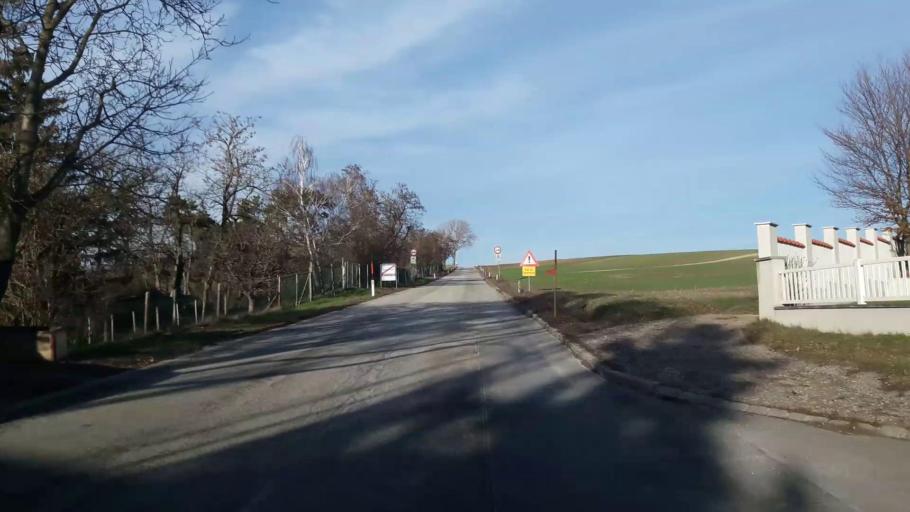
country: AT
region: Lower Austria
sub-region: Politischer Bezirk Ganserndorf
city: Auersthal
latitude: 48.3790
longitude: 16.6299
